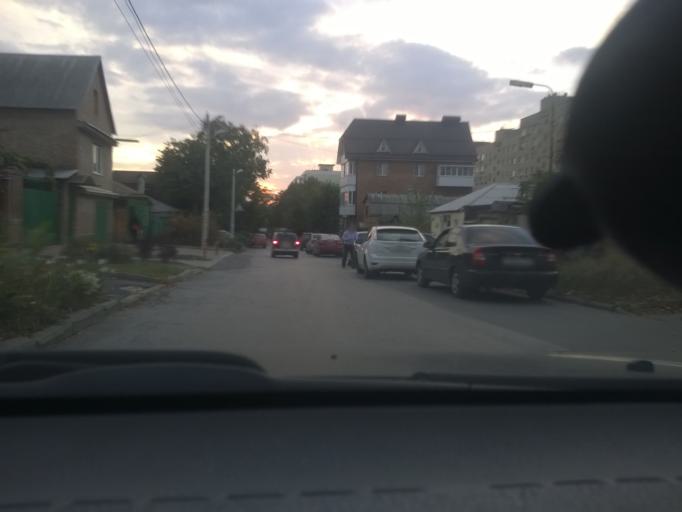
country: RU
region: Rostov
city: Rostov-na-Donu
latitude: 47.2296
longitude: 39.6846
